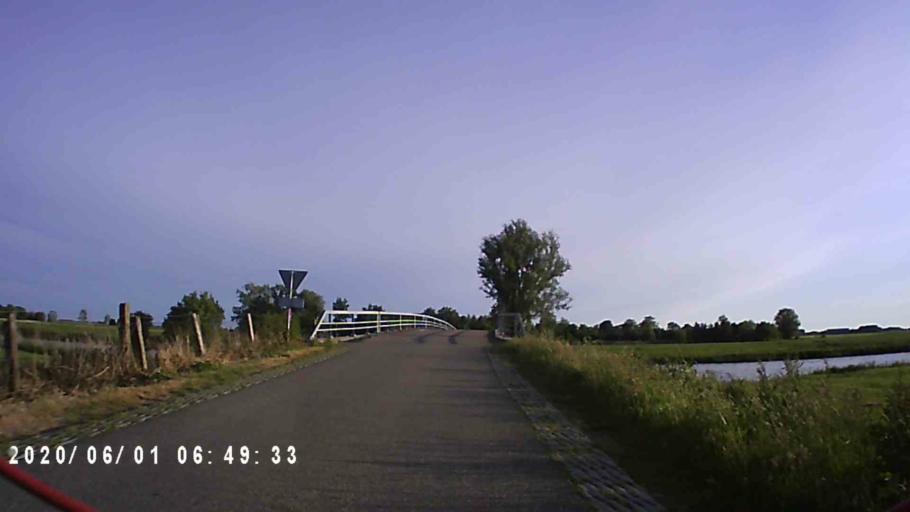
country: NL
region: Friesland
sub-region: Gemeente Kollumerland en Nieuwkruisland
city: Kollum
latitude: 53.2994
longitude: 6.1310
